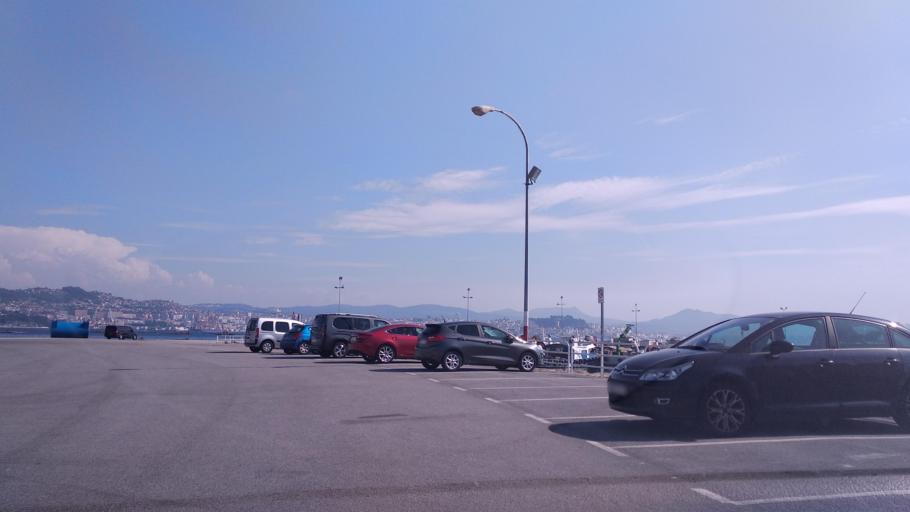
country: ES
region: Galicia
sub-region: Provincia de Pontevedra
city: Moana
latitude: 42.2740
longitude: -8.7367
